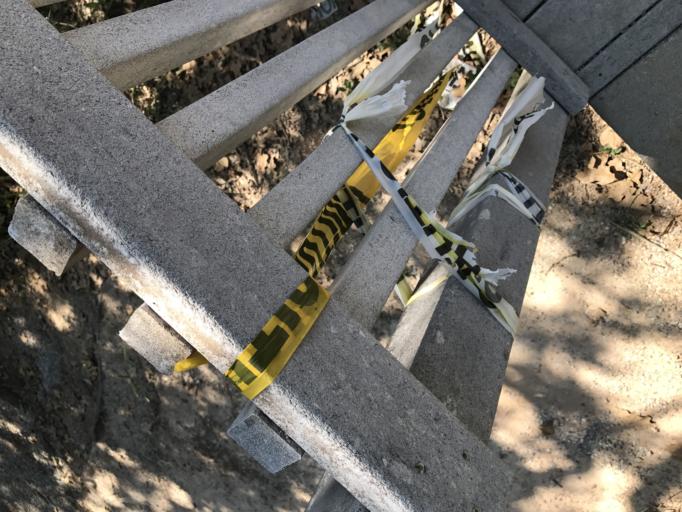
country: US
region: Texas
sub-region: Denton County
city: Corinth
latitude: 33.1528
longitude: -97.0455
